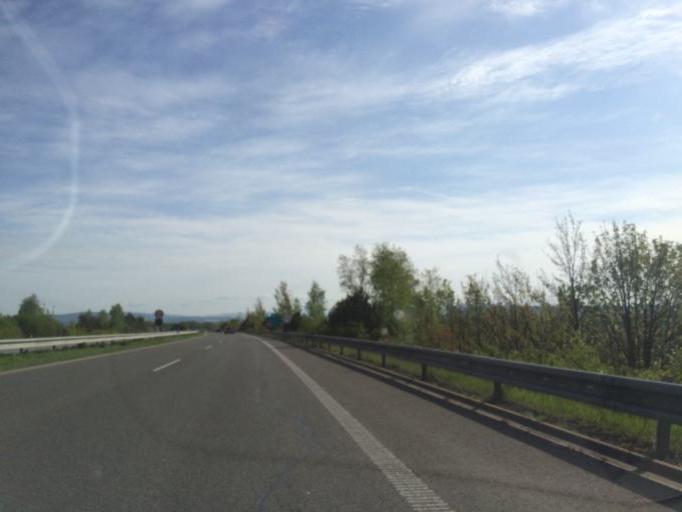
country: CZ
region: Central Bohemia
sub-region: Okres Mlada Boleslav
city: Zd'ar
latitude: 50.5424
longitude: 15.0369
